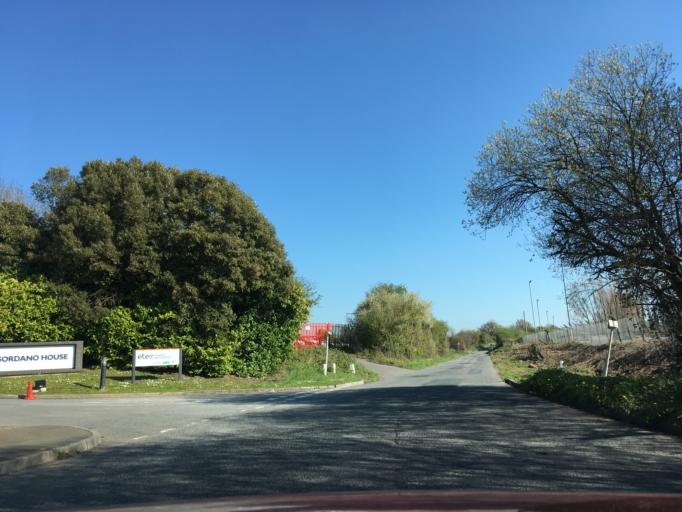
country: GB
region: England
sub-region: North Somerset
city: Easton-in-Gordano
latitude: 51.4839
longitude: -2.7088
